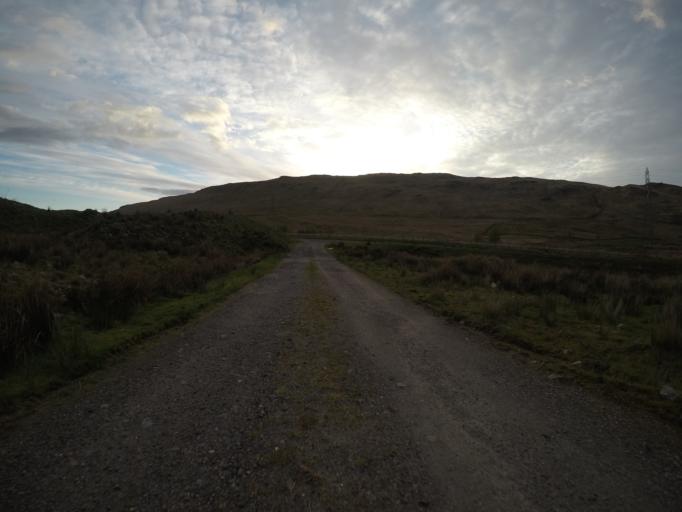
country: GB
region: Scotland
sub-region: Argyll and Bute
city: Garelochhead
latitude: 56.3797
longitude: -4.6408
